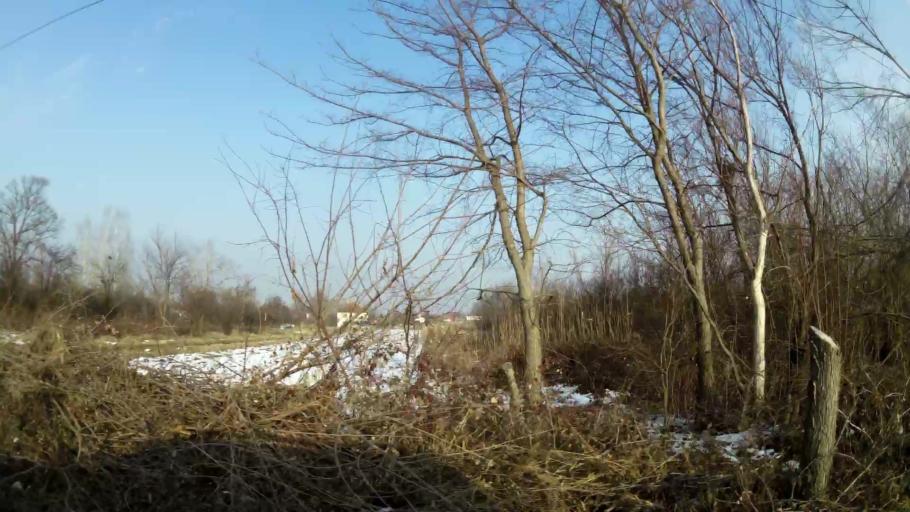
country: MK
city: Kadino
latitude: 41.9650
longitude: 21.5938
